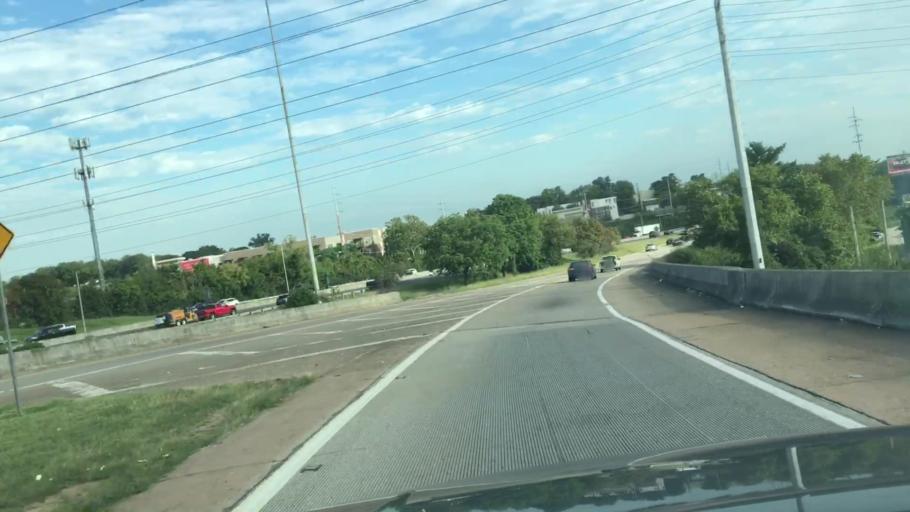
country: US
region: Tennessee
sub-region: Davidson County
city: Oak Hill
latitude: 36.1189
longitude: -86.7728
